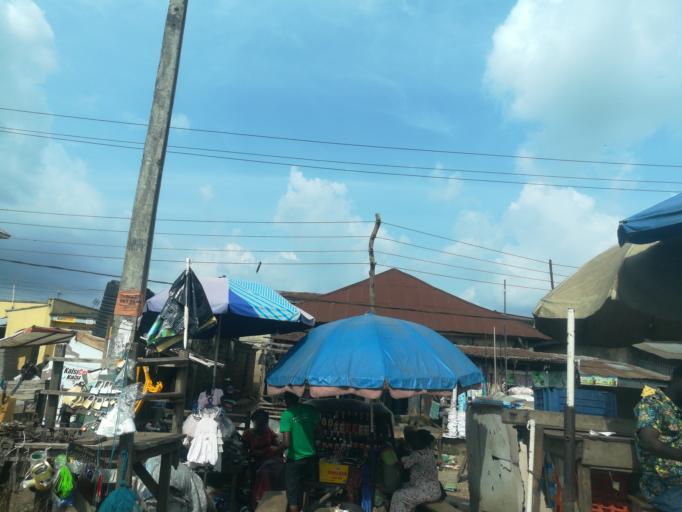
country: NG
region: Oyo
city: Ibadan
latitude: 7.3838
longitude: 3.8267
